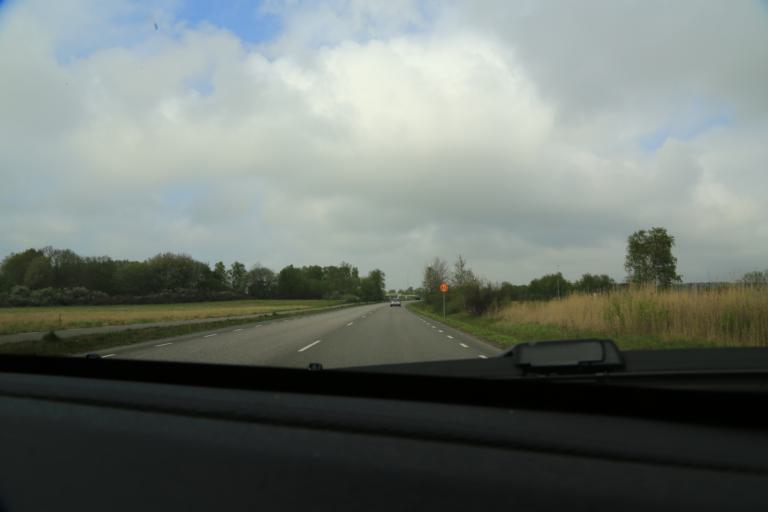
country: SE
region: Halland
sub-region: Kungsbacka Kommun
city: Frillesas
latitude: 57.2359
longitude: 12.1822
